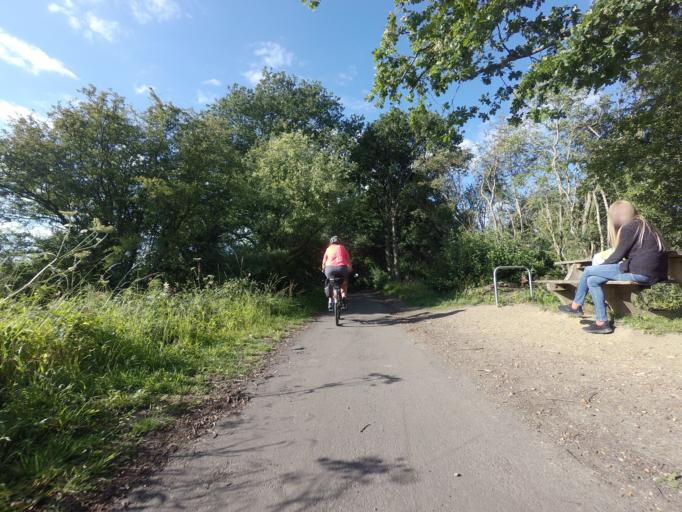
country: GB
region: England
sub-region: East Sussex
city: Hailsham
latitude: 50.8993
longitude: 0.2585
